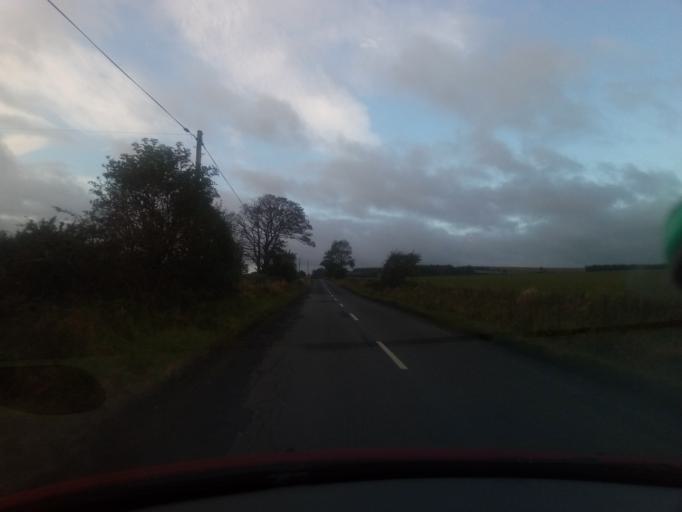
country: GB
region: Scotland
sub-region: The Scottish Borders
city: Jedburgh
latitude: 55.4437
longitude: -2.5821
